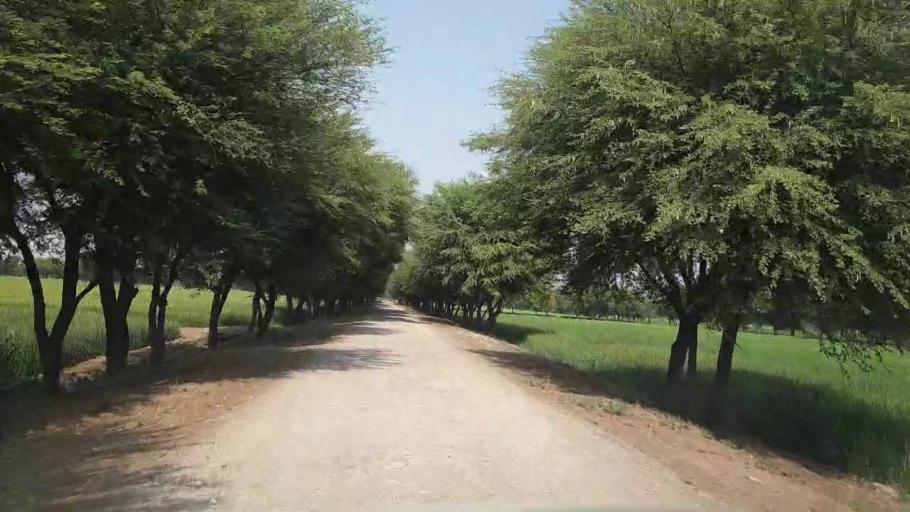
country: PK
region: Sindh
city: Dhoro Naro
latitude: 25.4823
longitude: 69.6218
